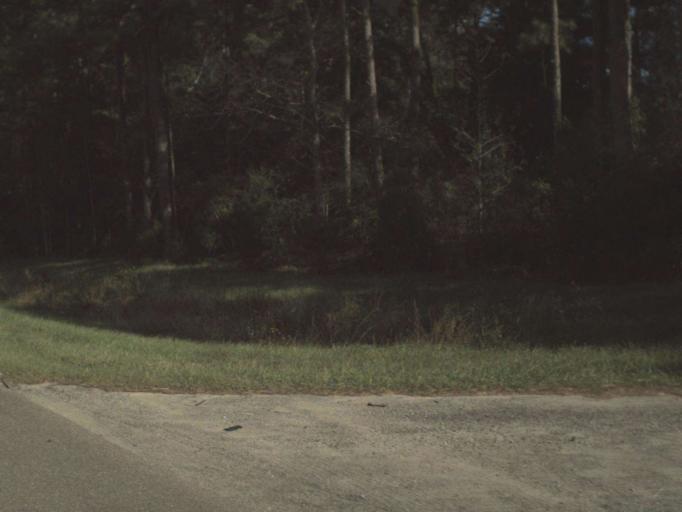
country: US
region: Florida
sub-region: Holmes County
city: Bonifay
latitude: 30.7766
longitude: -85.8044
